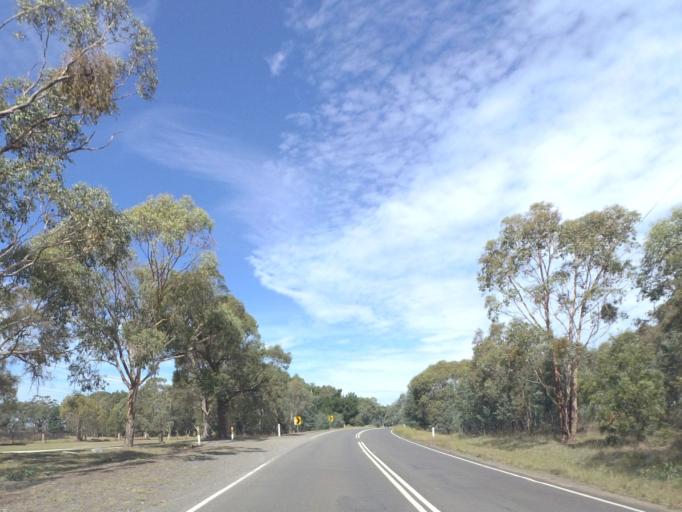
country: AU
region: Victoria
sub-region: Hume
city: Sunbury
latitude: -37.2991
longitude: 144.5130
